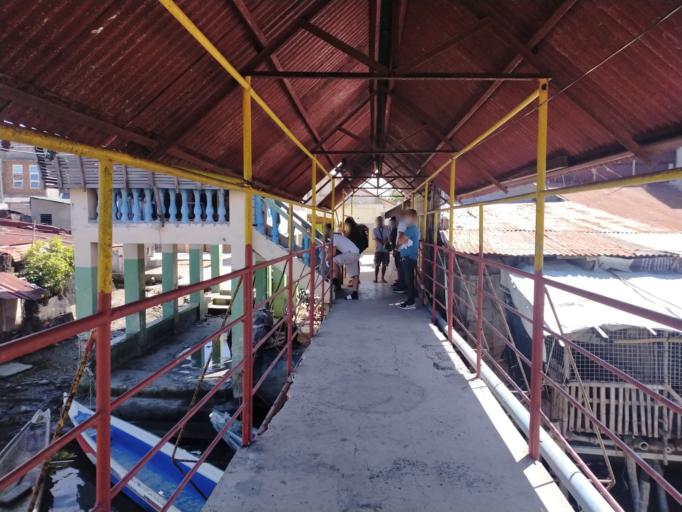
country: PH
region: Central Luzon
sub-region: Province of Pampanga
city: Malusac
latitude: 14.8444
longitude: 120.6170
